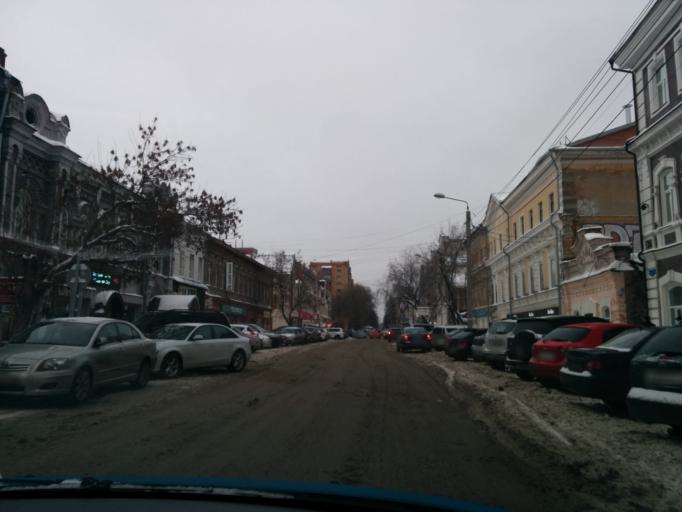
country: RU
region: Perm
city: Perm
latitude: 58.0143
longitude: 56.2366
